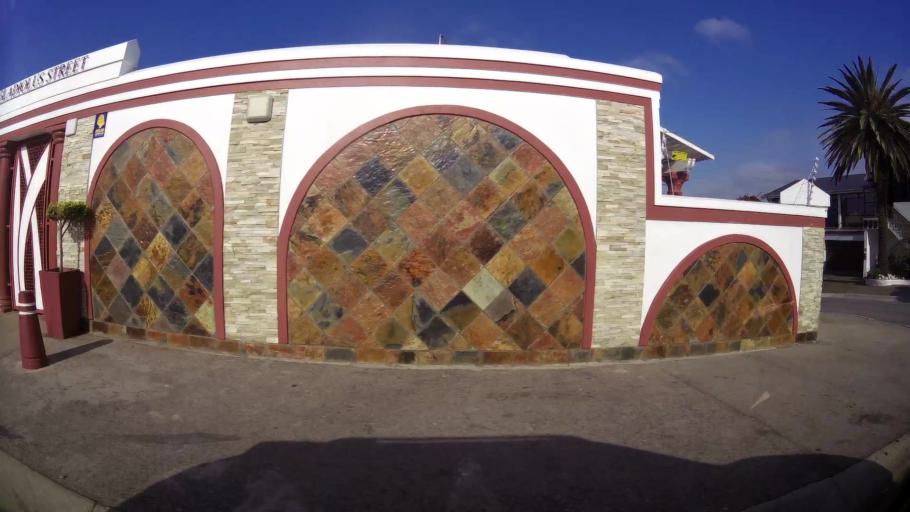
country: ZA
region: Eastern Cape
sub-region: Nelson Mandela Bay Metropolitan Municipality
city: Port Elizabeth
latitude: -33.9247
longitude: 25.5429
